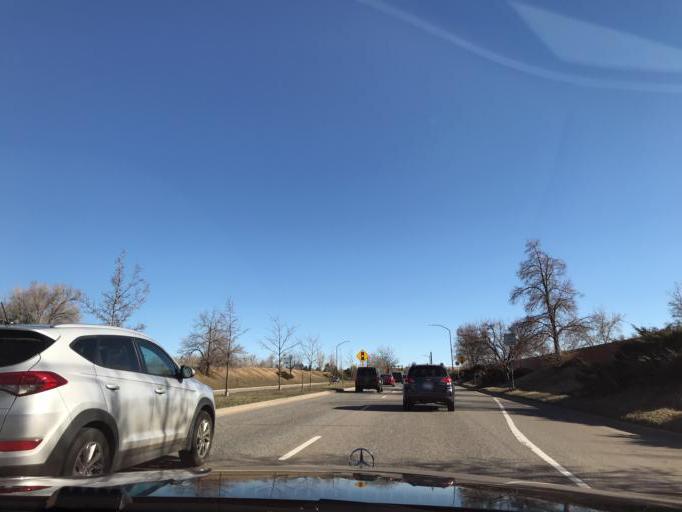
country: US
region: Colorado
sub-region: Boulder County
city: Boulder
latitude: 40.0023
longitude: -105.2347
